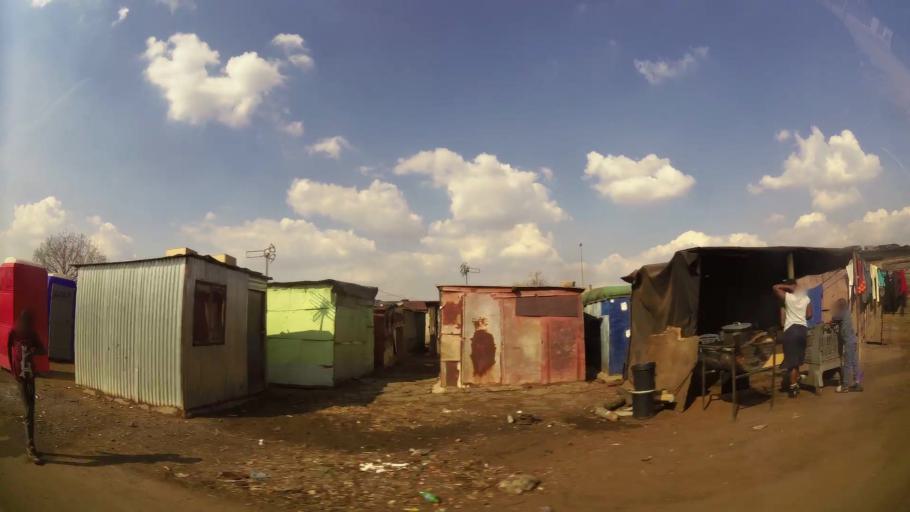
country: ZA
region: Gauteng
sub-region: Ekurhuleni Metropolitan Municipality
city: Germiston
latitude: -26.3343
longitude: 28.1393
